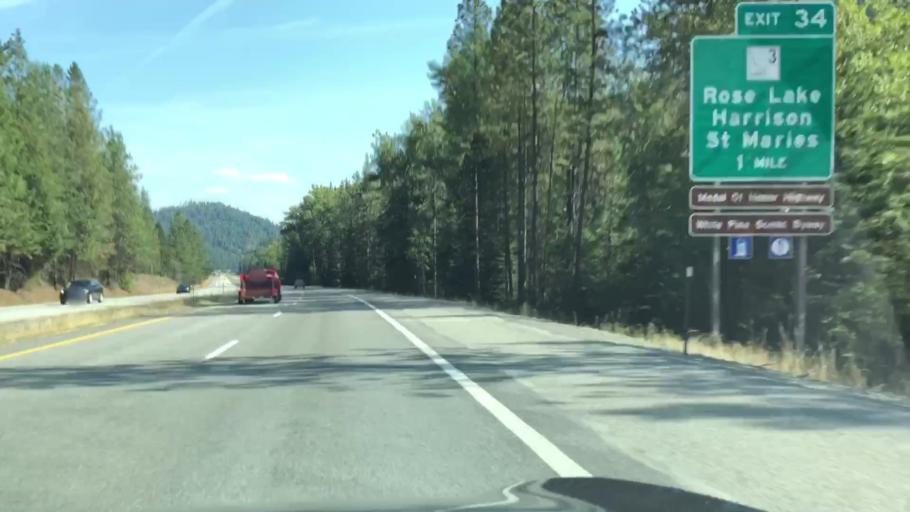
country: US
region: Idaho
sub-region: Shoshone County
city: Pinehurst
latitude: 47.5824
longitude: -116.4671
